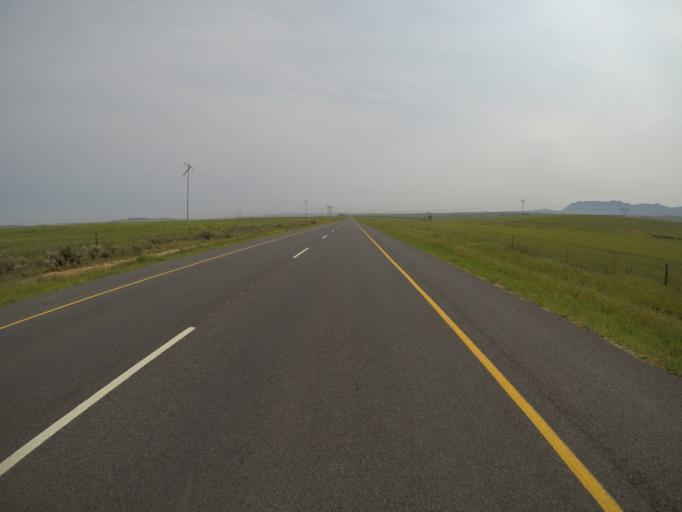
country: ZA
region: Western Cape
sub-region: West Coast District Municipality
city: Malmesbury
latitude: -33.4977
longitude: 18.8312
